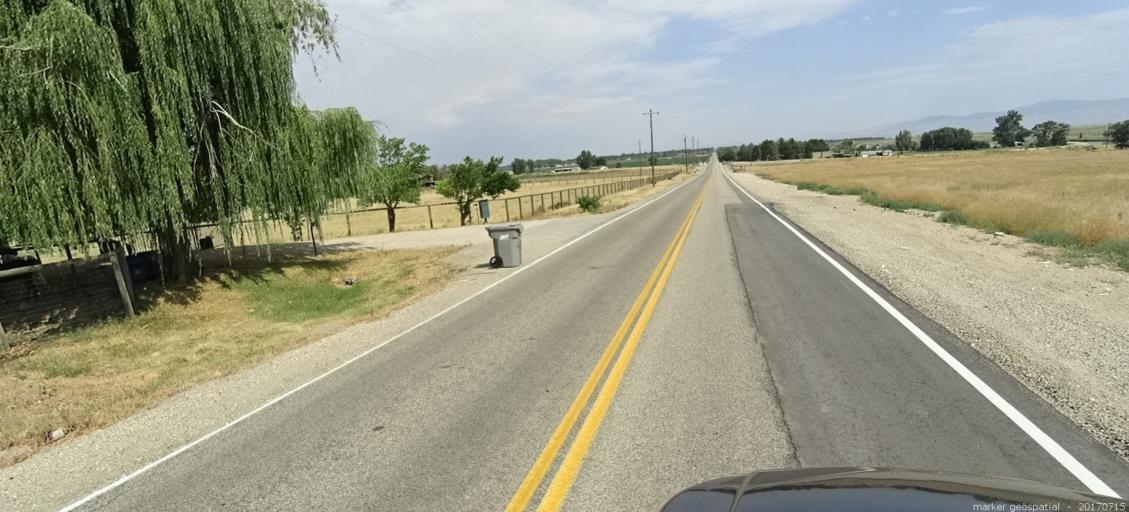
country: US
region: Idaho
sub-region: Ada County
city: Garden City
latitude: 43.5265
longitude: -116.2742
